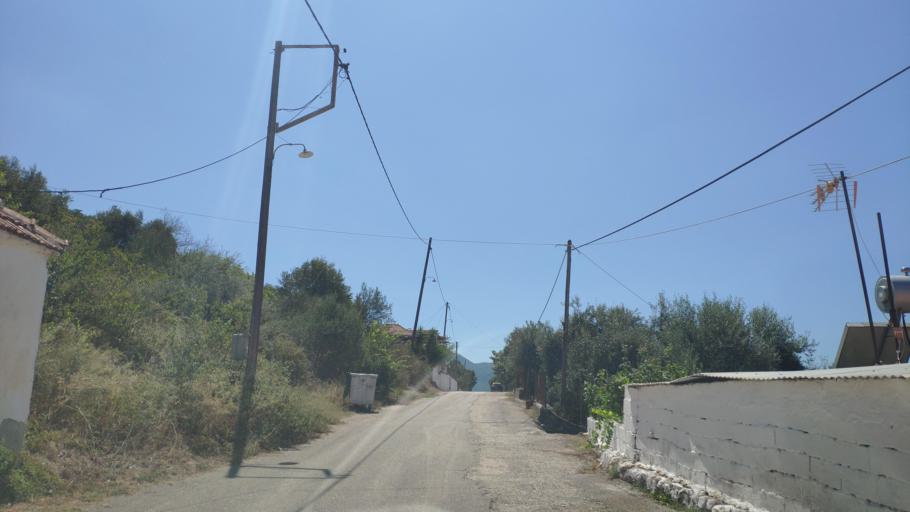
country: GR
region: Epirus
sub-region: Nomos Prevezis
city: Kanalaki
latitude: 39.2751
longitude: 20.5990
